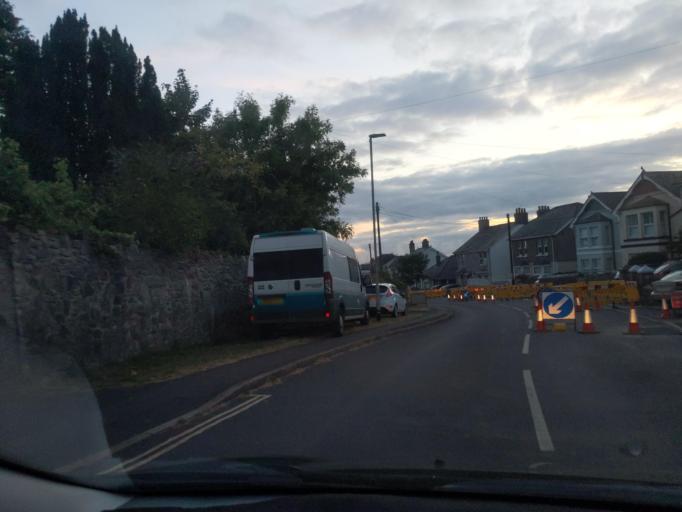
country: GB
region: England
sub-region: Plymouth
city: Plymstock
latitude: 50.3605
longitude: -4.1023
